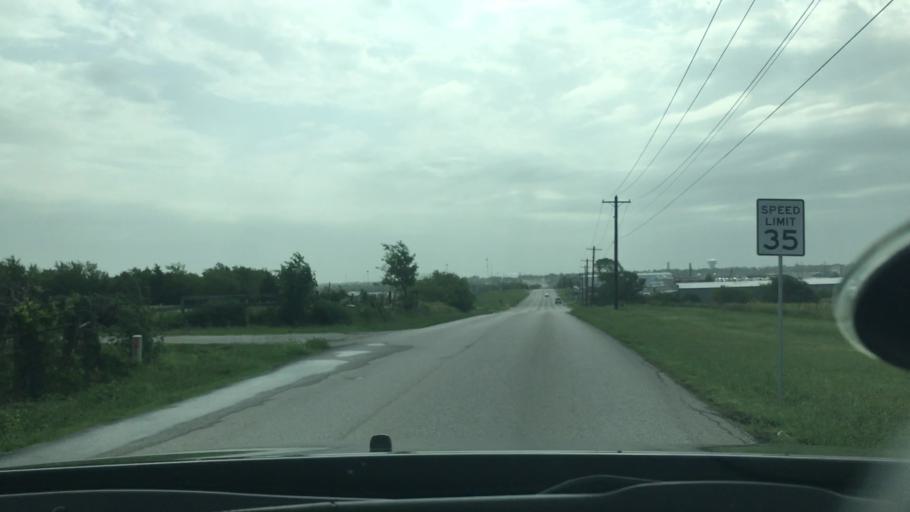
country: US
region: Oklahoma
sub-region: Carter County
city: Ardmore
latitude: 34.2020
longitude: -97.1764
